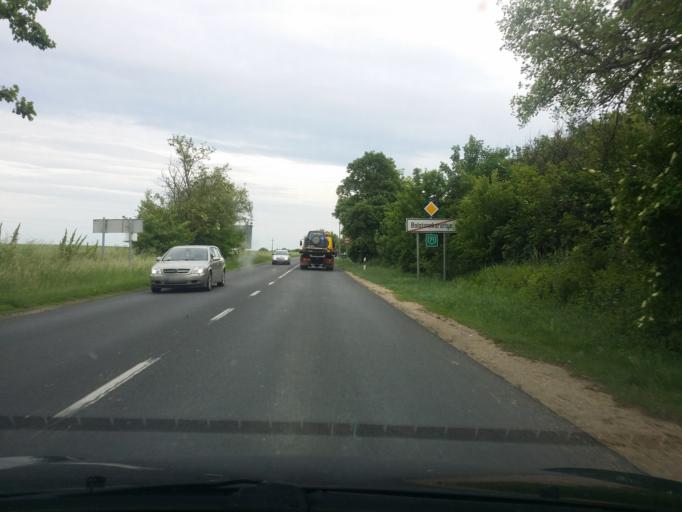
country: HU
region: Veszprem
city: Balatonkenese
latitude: 47.0098
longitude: 18.1728
